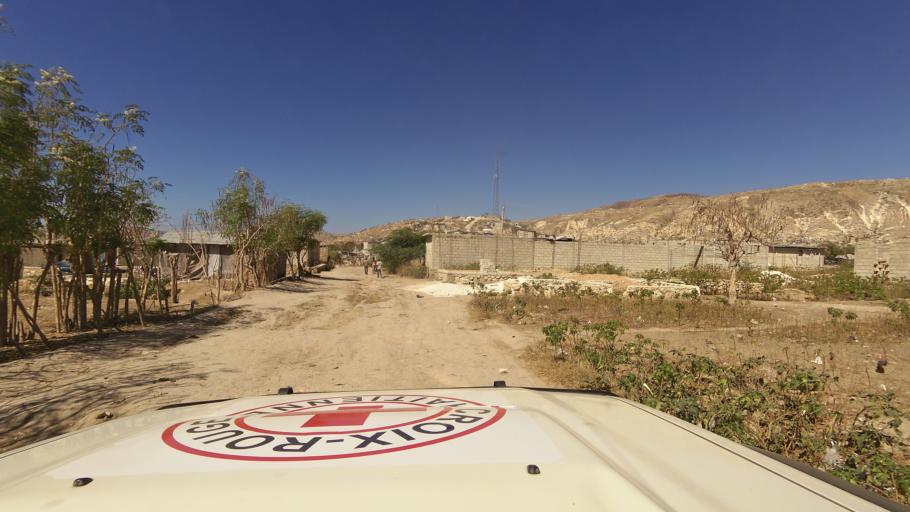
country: HT
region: Ouest
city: Croix des Bouquets
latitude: 18.6611
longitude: -72.2536
